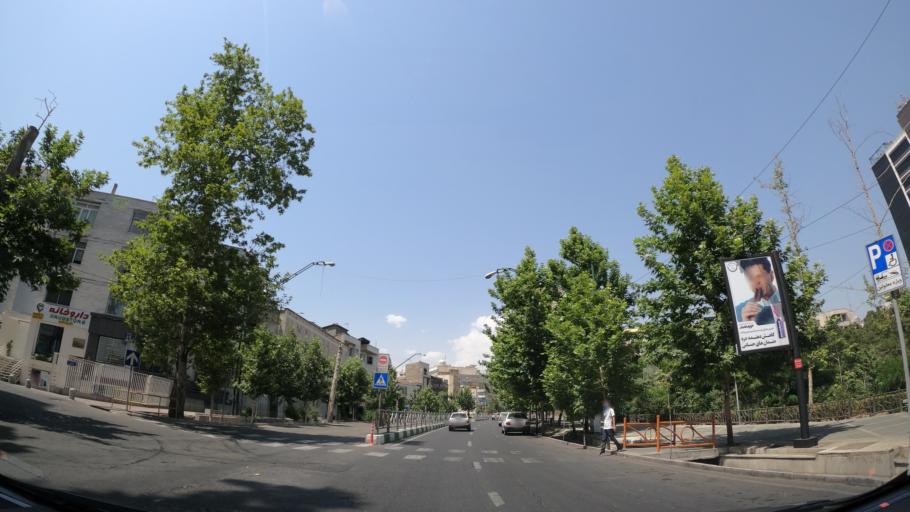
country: IR
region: Tehran
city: Tehran
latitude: 35.7377
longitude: 51.4091
